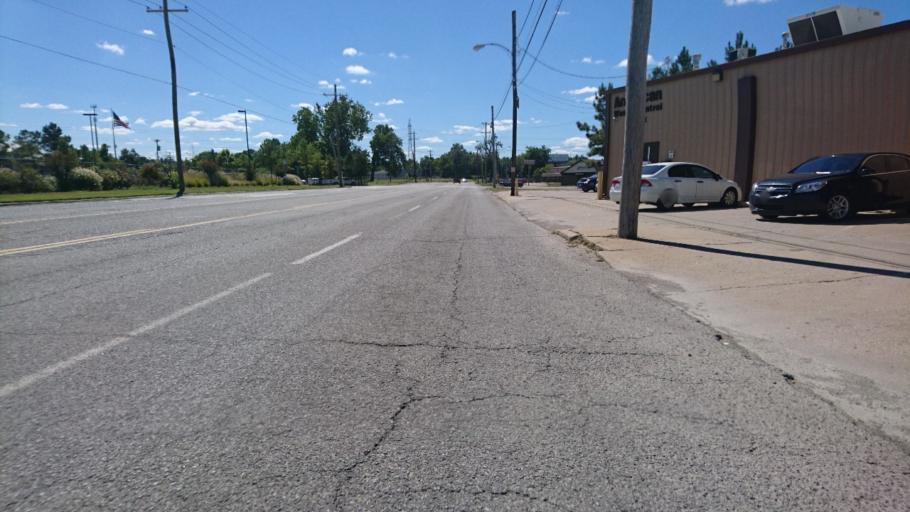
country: US
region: Oklahoma
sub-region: Tulsa County
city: Tulsa
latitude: 36.1148
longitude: -96.0089
